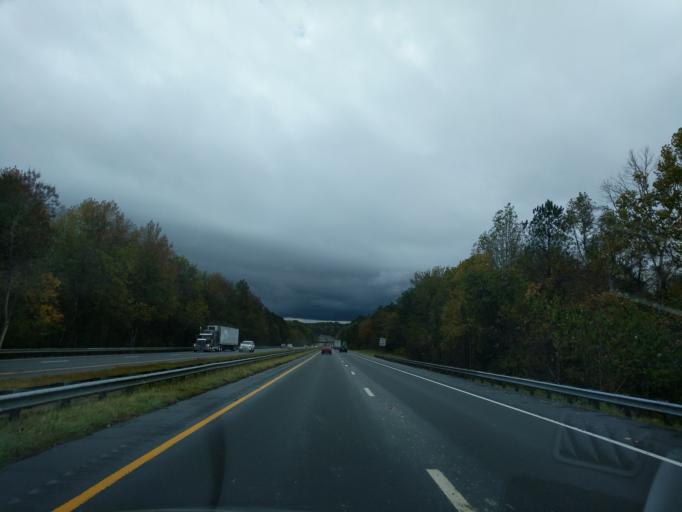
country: US
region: North Carolina
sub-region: Orange County
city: Hillsborough
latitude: 36.0441
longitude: -79.0394
